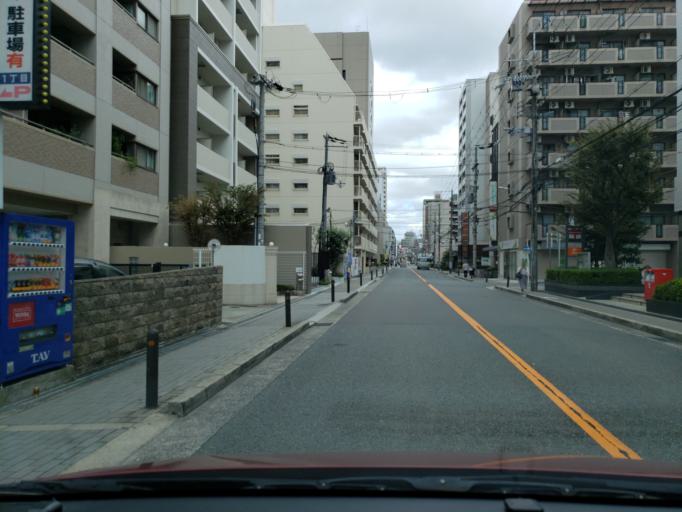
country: JP
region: Osaka
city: Suita
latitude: 34.7606
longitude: 135.4983
